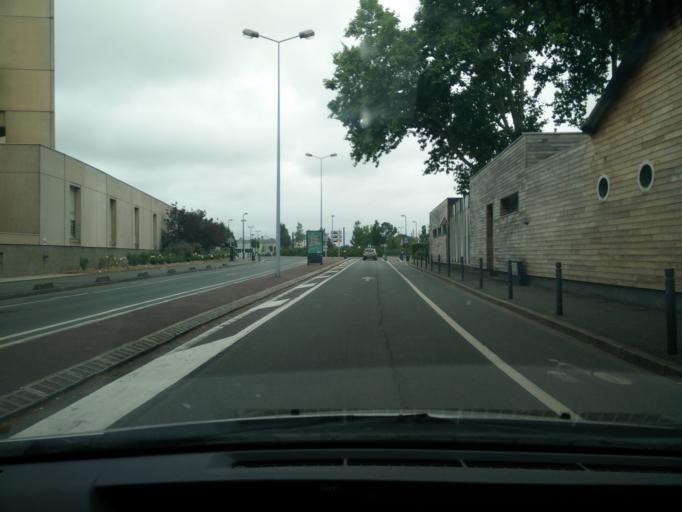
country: FR
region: Pays de la Loire
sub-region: Departement de Maine-et-Loire
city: Angers
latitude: 47.4796
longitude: -0.5554
